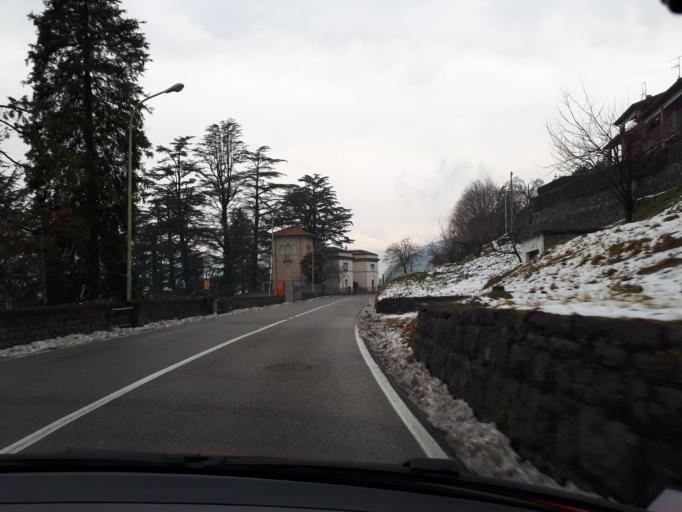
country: IT
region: Lombardy
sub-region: Provincia di Lecco
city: Mandello del Lario
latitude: 45.9306
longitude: 9.3120
